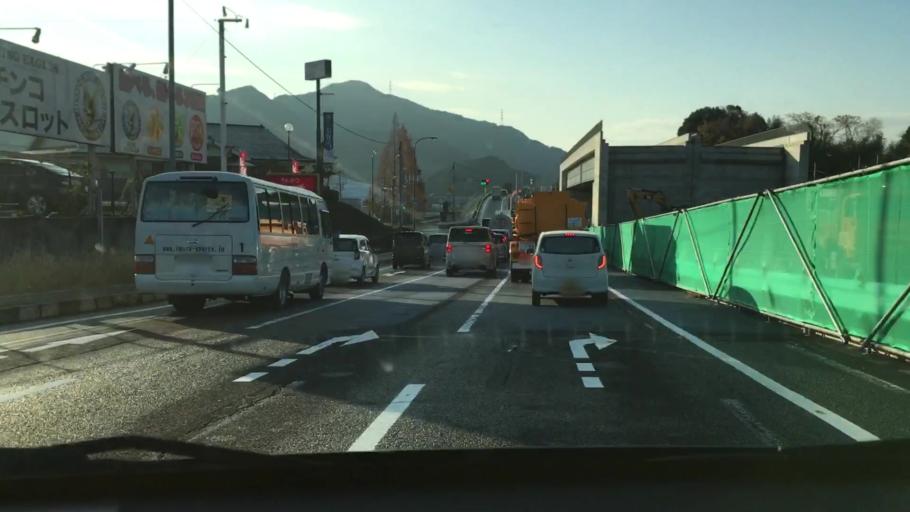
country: JP
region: Nagasaki
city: Sasebo
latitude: 33.1173
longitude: 129.7930
